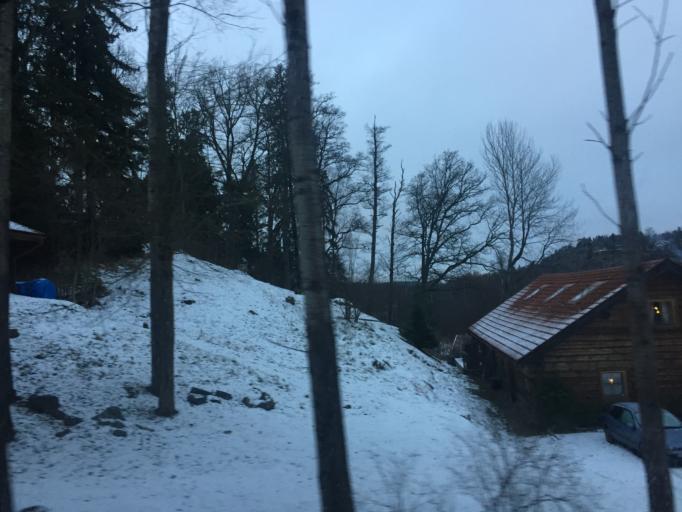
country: SE
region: Stockholm
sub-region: Botkyrka Kommun
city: Tullinge
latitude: 59.2010
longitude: 17.8877
